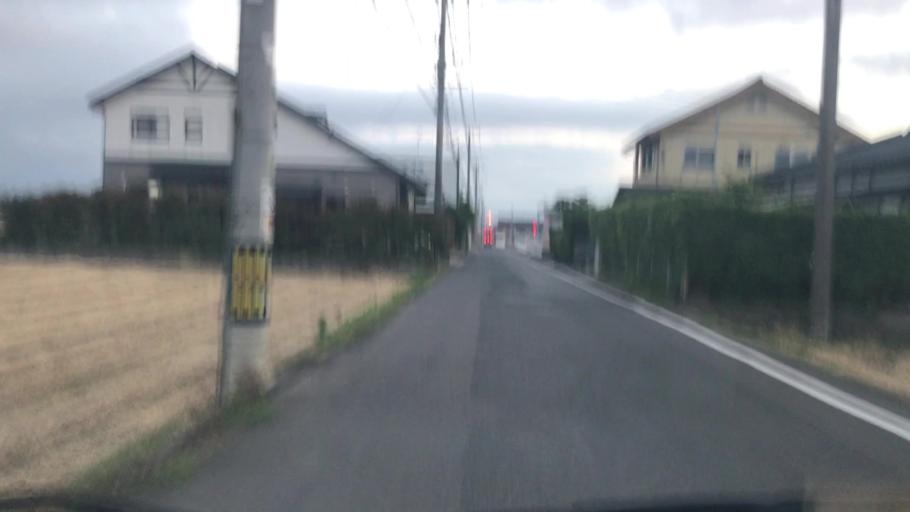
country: JP
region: Saga Prefecture
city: Saga-shi
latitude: 33.2300
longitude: 130.3019
